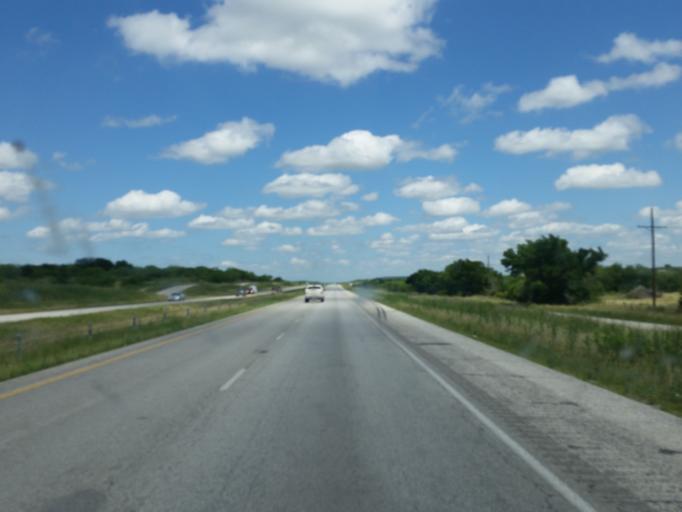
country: US
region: Texas
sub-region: Callahan County
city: Baird
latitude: 32.3838
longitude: -99.2855
